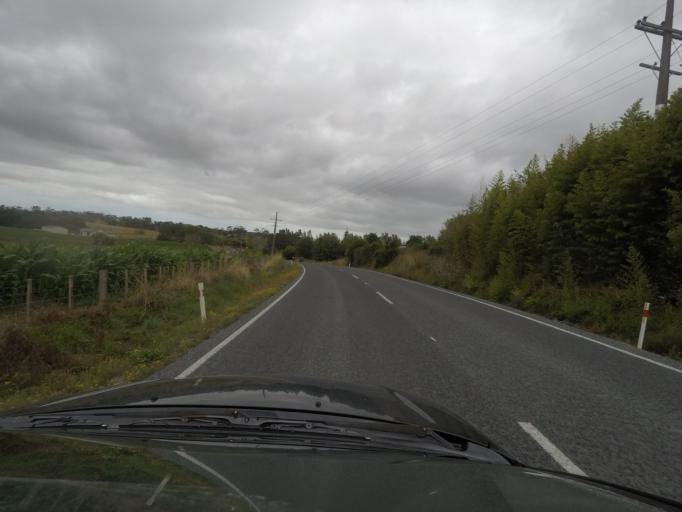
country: NZ
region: Auckland
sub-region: Auckland
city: Wellsford
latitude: -36.2816
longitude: 174.5702
